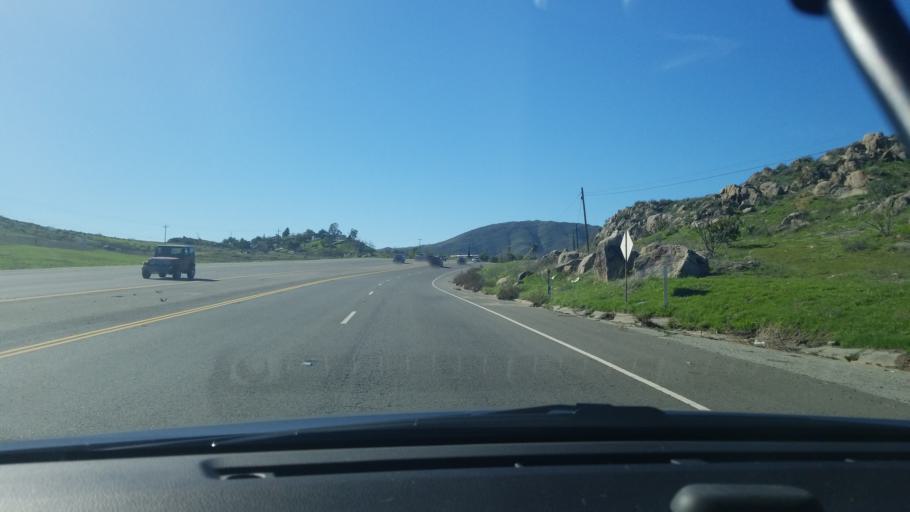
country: US
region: California
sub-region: Riverside County
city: Green Acres
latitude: 33.7421
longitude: -117.0640
